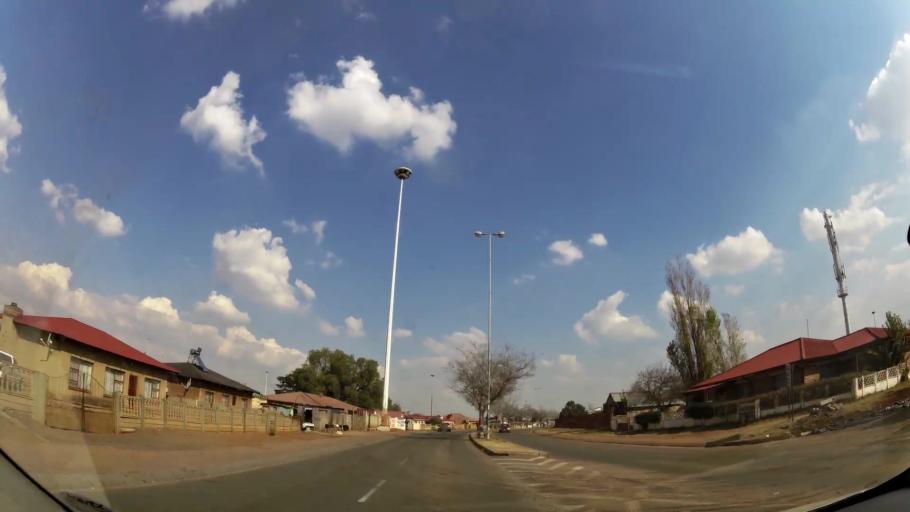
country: ZA
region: Gauteng
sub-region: Ekurhuleni Metropolitan Municipality
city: Germiston
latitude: -26.3225
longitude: 28.1563
